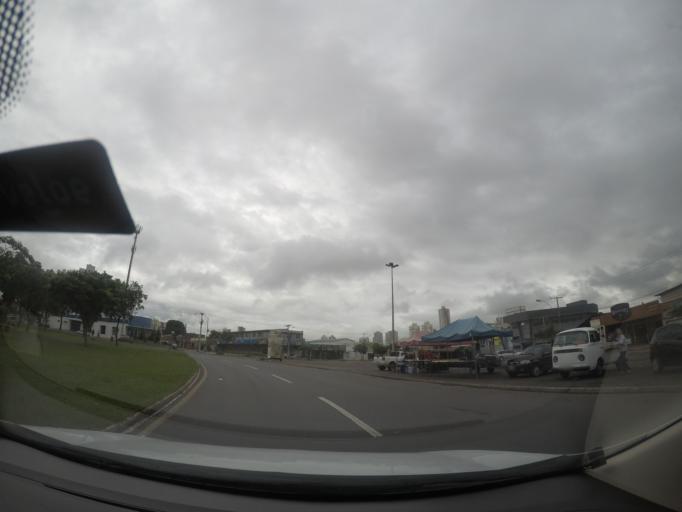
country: BR
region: Goias
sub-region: Goiania
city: Goiania
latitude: -16.7285
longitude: -49.2787
